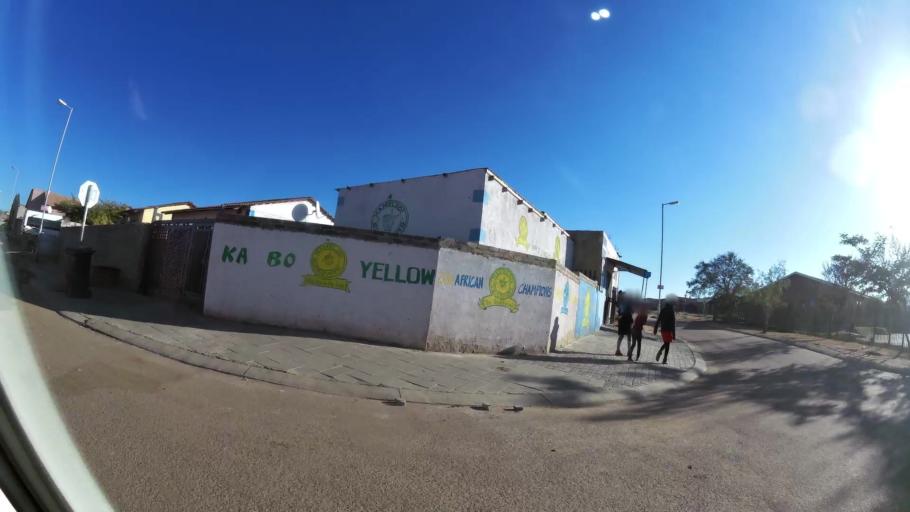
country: ZA
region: Gauteng
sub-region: City of Johannesburg Metropolitan Municipality
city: Midrand
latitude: -25.9041
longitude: 28.0996
